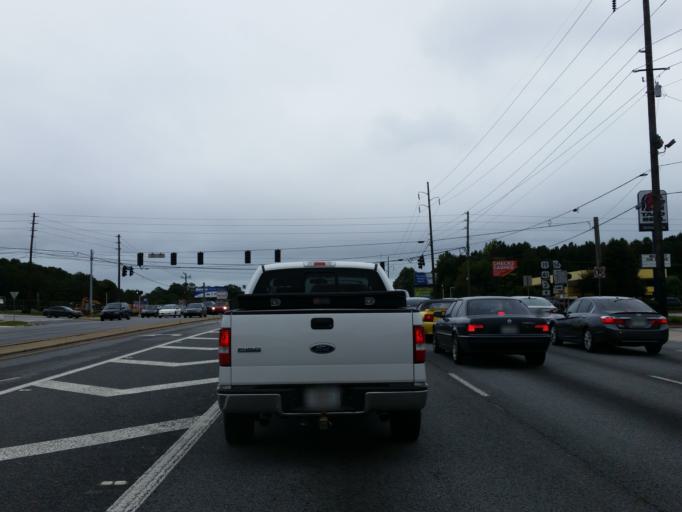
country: US
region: Georgia
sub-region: Clayton County
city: Jonesboro
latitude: 33.5330
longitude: -84.3641
